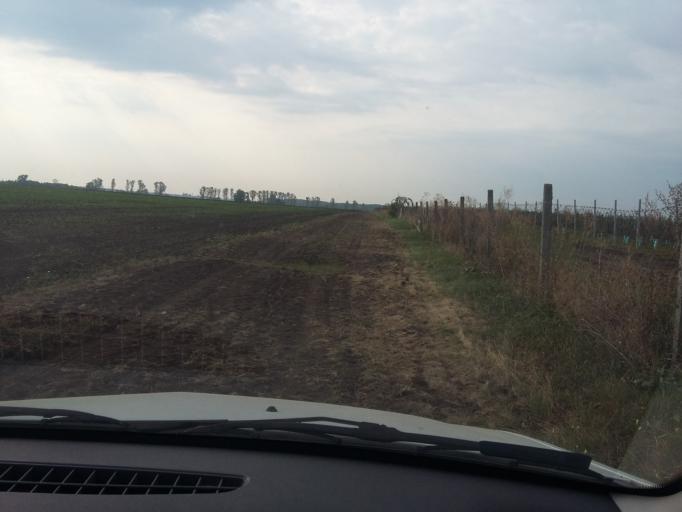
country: HU
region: Borsod-Abauj-Zemplen
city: Taktaharkany
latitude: 48.1281
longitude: 21.1071
